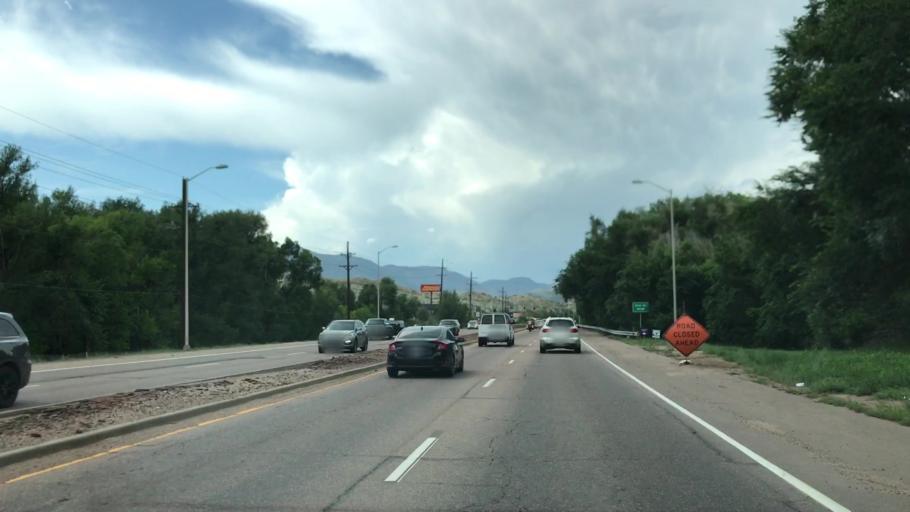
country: US
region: Colorado
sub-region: El Paso County
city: Colorado Springs
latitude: 38.8388
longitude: -104.8560
